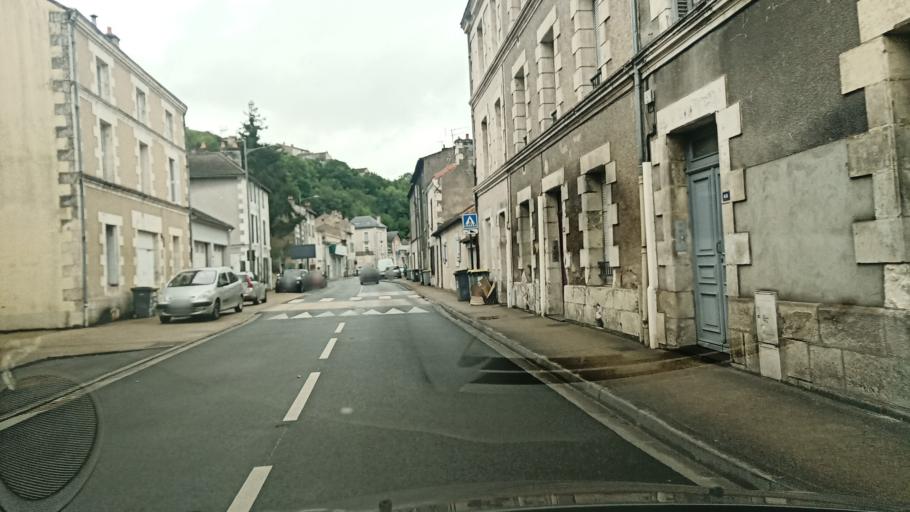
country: FR
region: Poitou-Charentes
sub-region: Departement de la Vienne
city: Poitiers
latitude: 46.5923
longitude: 0.3376
